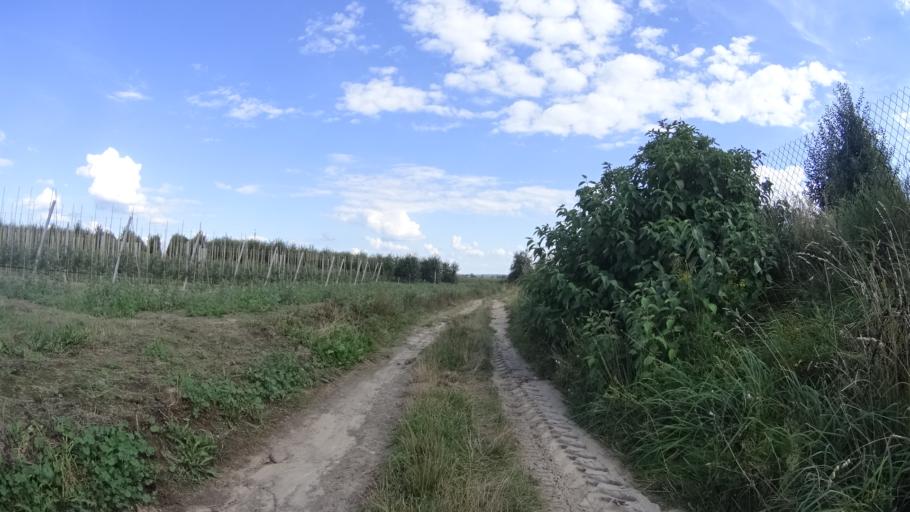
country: PL
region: Masovian Voivodeship
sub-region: Powiat bialobrzeski
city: Wysmierzyce
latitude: 51.6687
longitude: 20.8077
